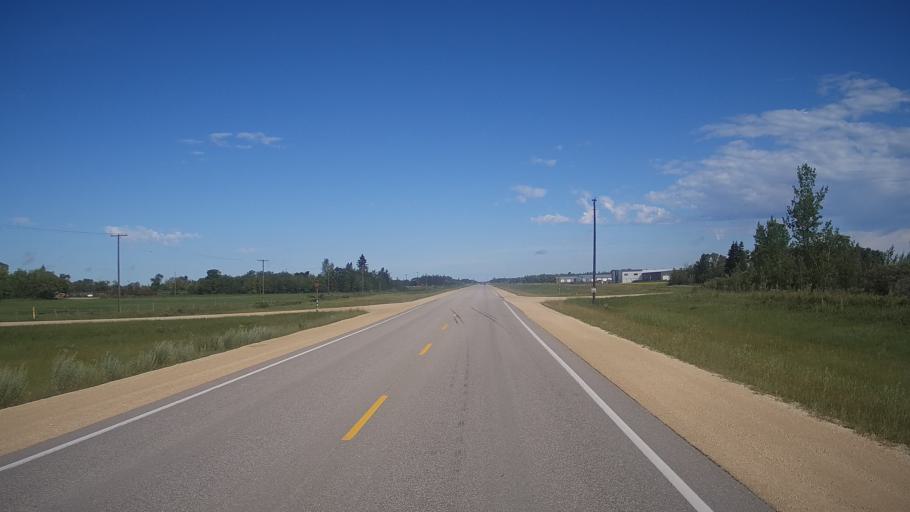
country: CA
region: Manitoba
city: Stonewall
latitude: 50.1942
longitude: -97.6424
